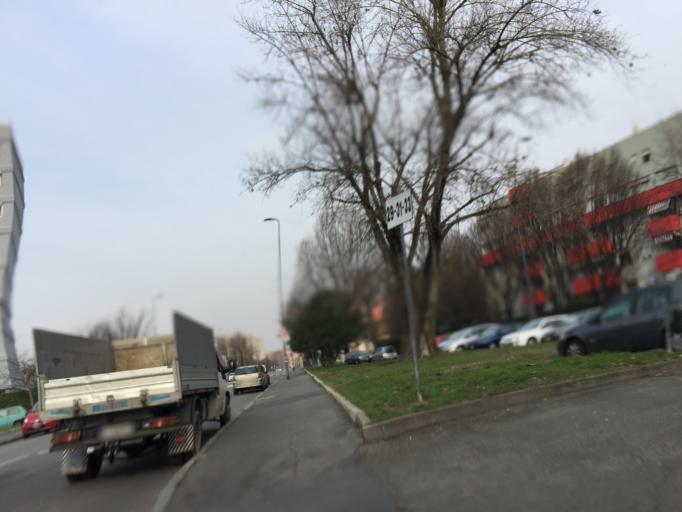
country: IT
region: Lombardy
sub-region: Citta metropolitana di Milano
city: Romano Banco
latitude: 45.4313
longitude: 9.1485
